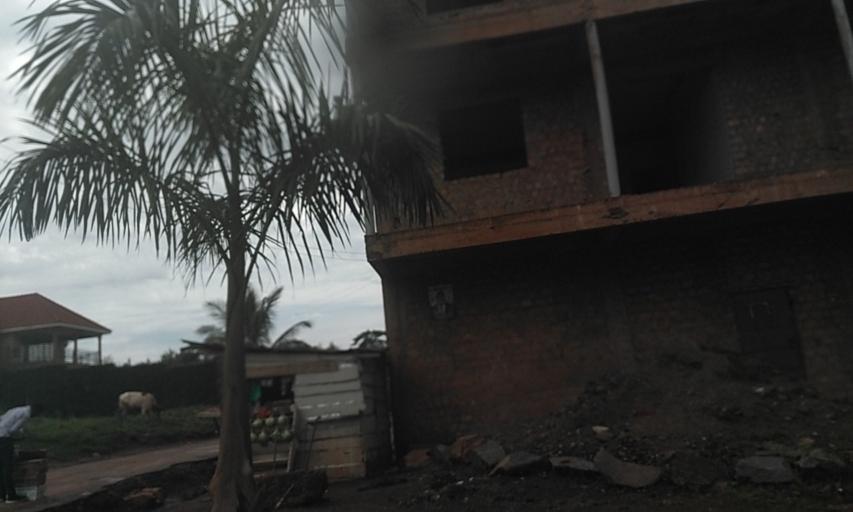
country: UG
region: Central Region
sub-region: Wakiso District
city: Kireka
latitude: 0.3653
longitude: 32.6377
